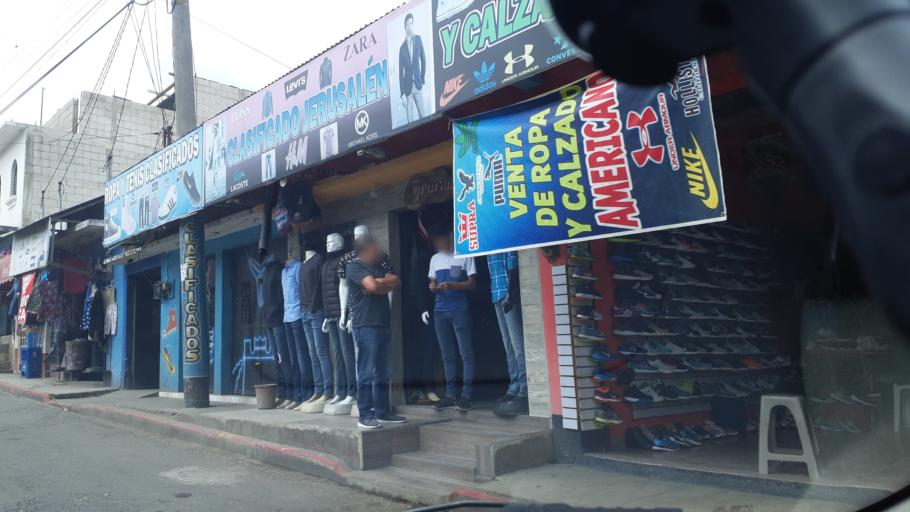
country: GT
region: Chimaltenango
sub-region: Municipio de Chimaltenango
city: Chimaltenango
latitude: 14.6628
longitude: -90.8177
